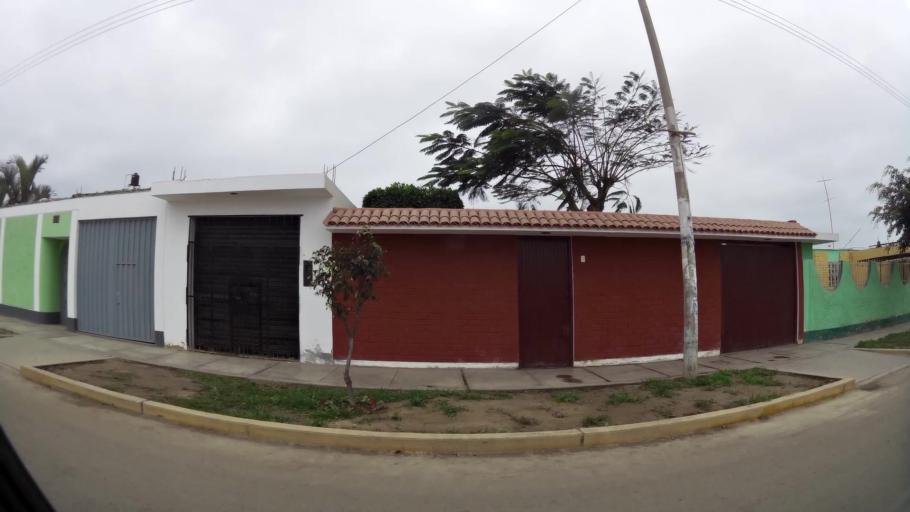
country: PE
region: Lima
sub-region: Barranca
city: Paramonga
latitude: -10.6757
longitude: -77.8127
